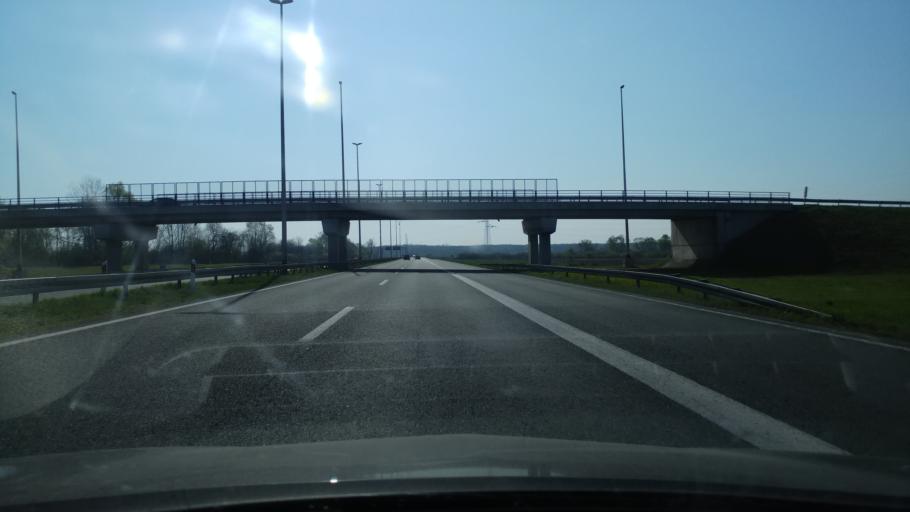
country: HR
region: Sisacko-Moslavacka
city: Kutina
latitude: 45.4588
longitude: 16.7601
